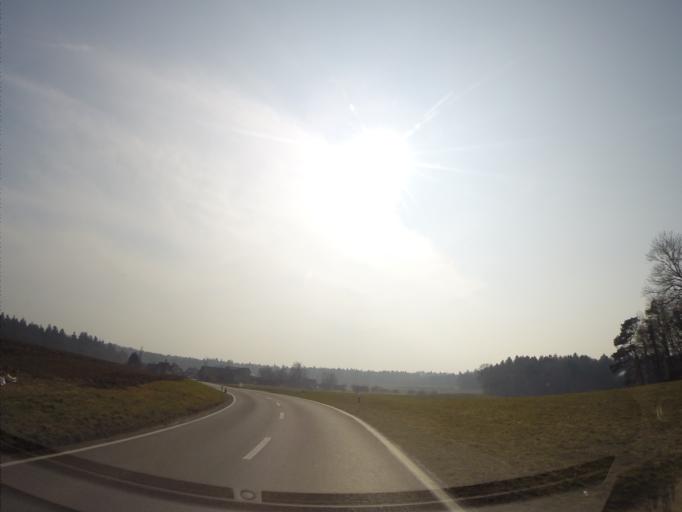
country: CH
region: Thurgau
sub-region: Frauenfeld District
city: Diessenhofen
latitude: 47.6506
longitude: 8.7251
